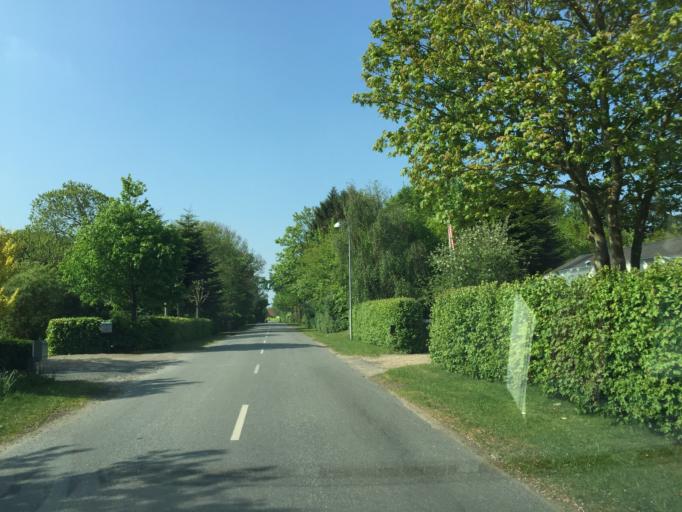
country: DK
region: South Denmark
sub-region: Esbjerg Kommune
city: Ribe
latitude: 55.2942
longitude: 8.6835
